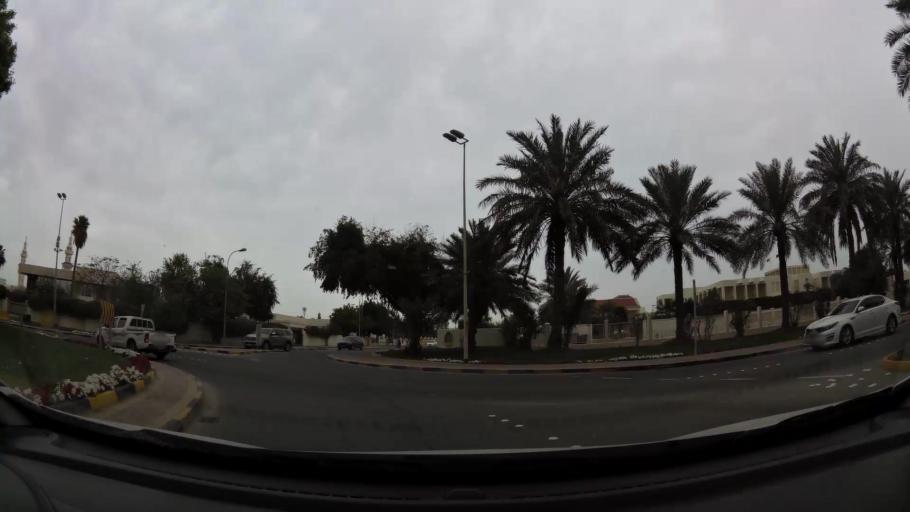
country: BH
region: Northern
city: Ar Rifa'
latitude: 26.1212
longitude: 50.5362
